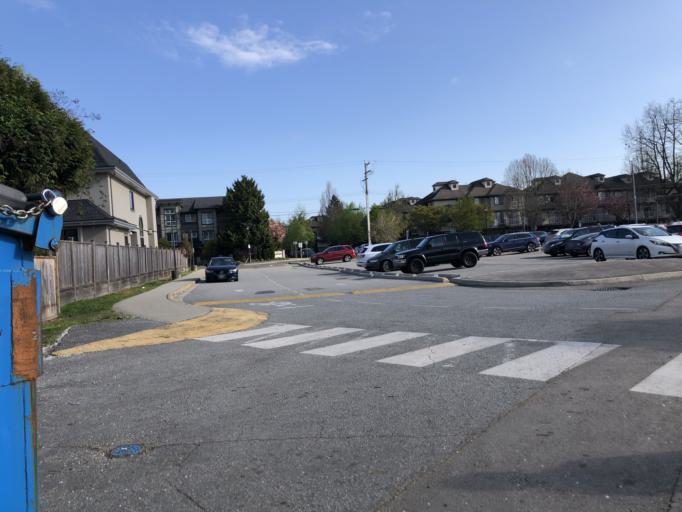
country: CA
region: British Columbia
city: Richmond
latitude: 49.1650
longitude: -123.1196
